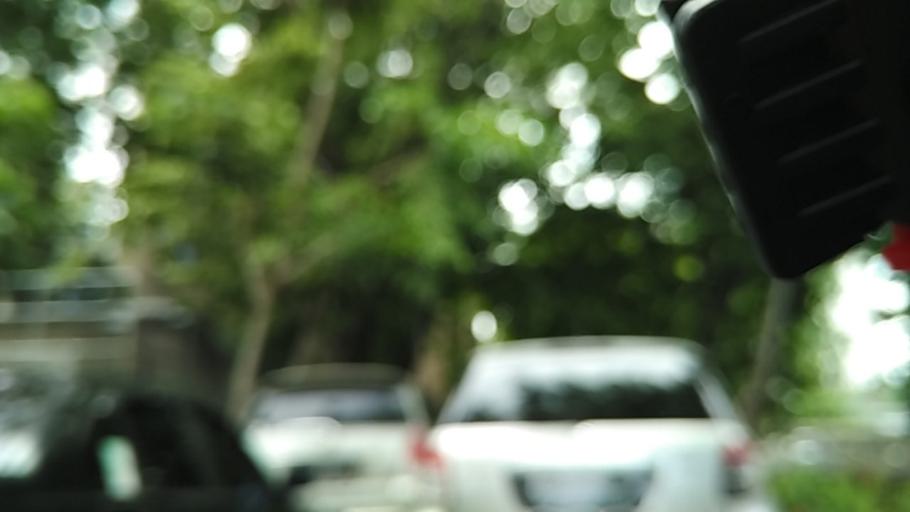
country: ID
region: Central Java
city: Semarang
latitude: -6.9839
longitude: 110.4141
